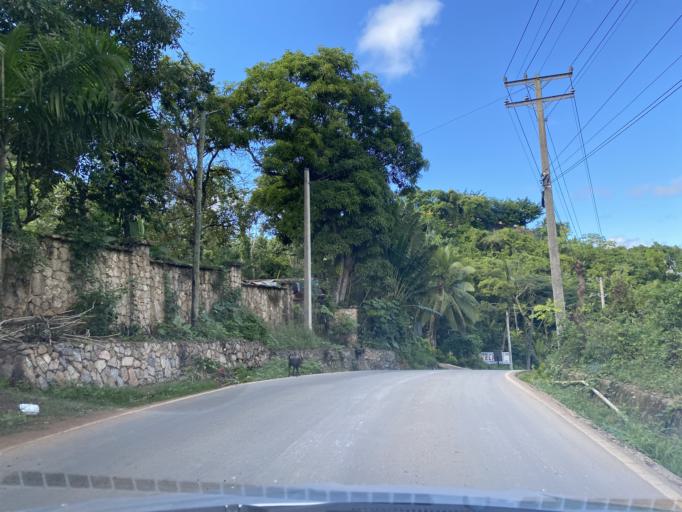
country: DO
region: Samana
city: Las Terrenas
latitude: 19.2978
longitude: -69.5523
